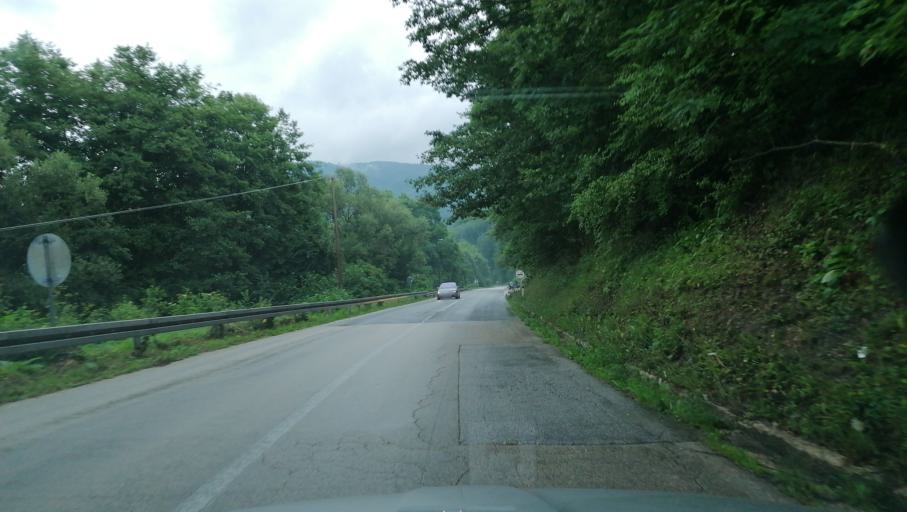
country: RS
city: Durici
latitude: 43.8010
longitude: 19.5053
